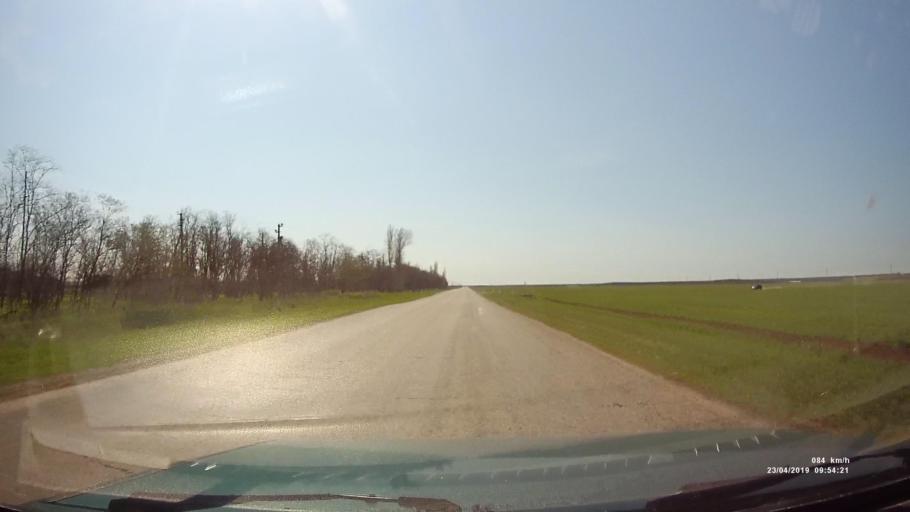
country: RU
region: Rostov
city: Orlovskiy
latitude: 46.8220
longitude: 42.0547
